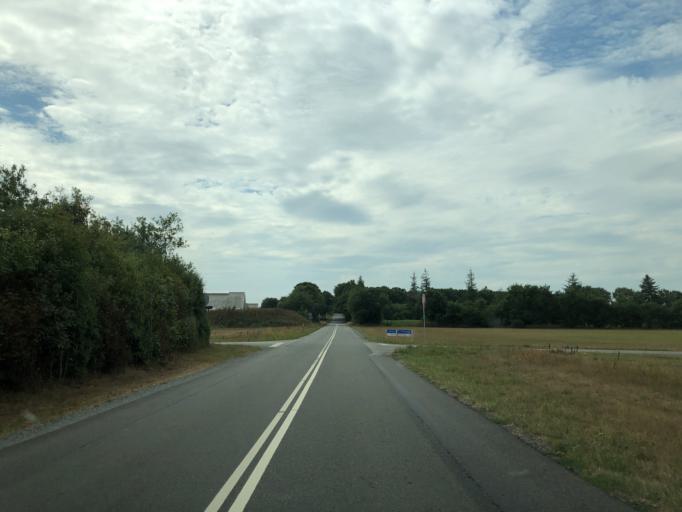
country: DK
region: South Denmark
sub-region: Vejle Kommune
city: Egtved
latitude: 55.6178
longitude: 9.1916
